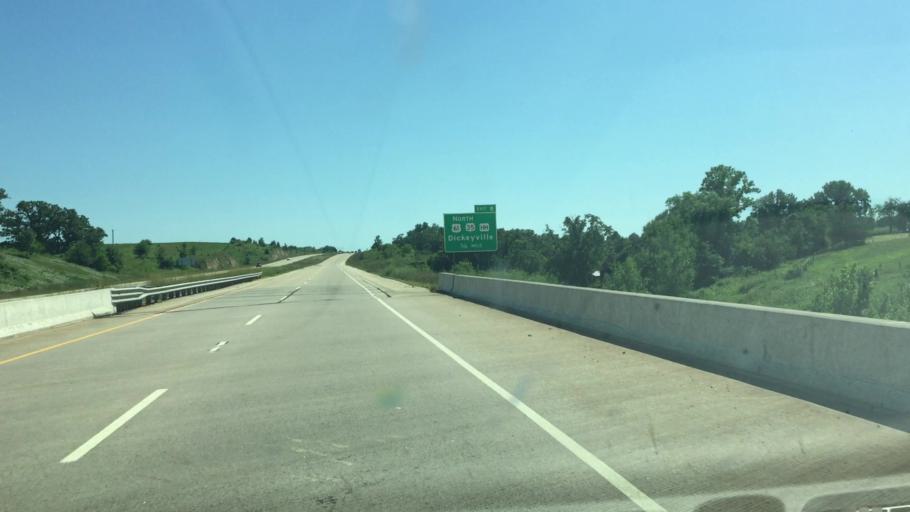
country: US
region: Wisconsin
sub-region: Grant County
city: Dickeyville
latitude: 42.6322
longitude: -90.5804
